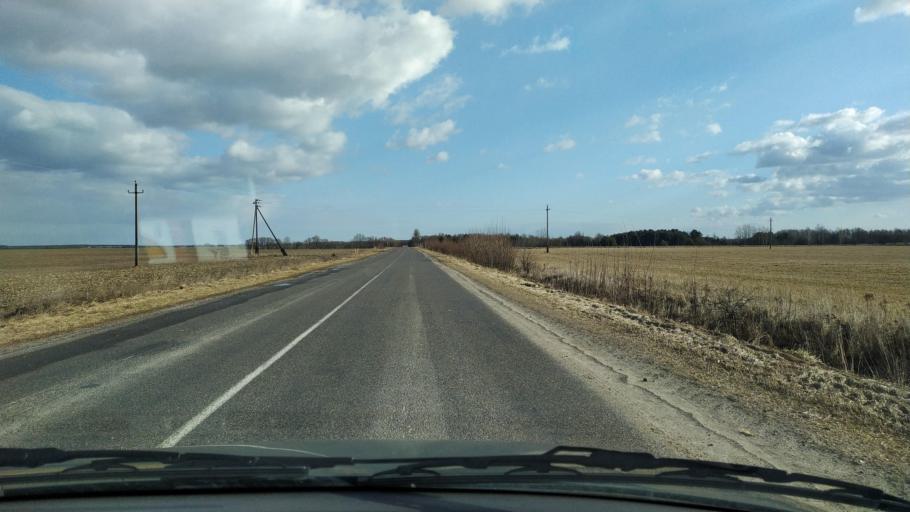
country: BY
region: Brest
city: Kamyanyets
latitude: 52.4261
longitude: 23.8118
